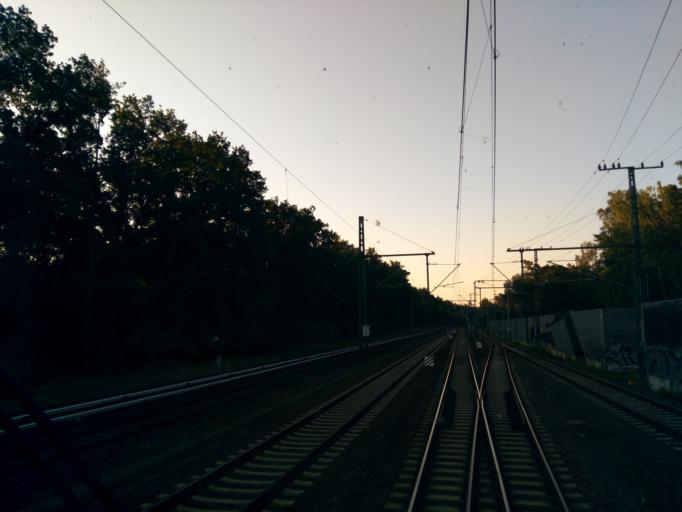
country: DE
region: Berlin
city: Bohnsdorf
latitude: 52.3993
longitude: 13.5935
